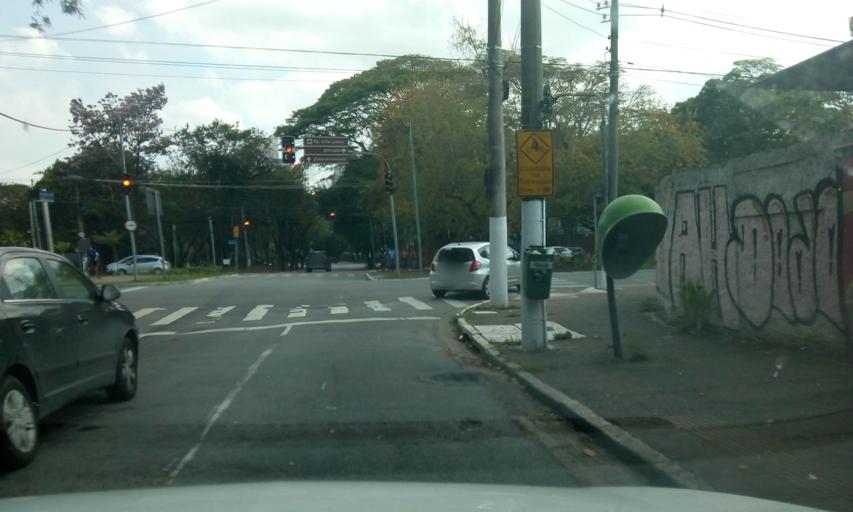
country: BR
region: Sao Paulo
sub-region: Osasco
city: Osasco
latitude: -23.5473
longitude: -46.7154
